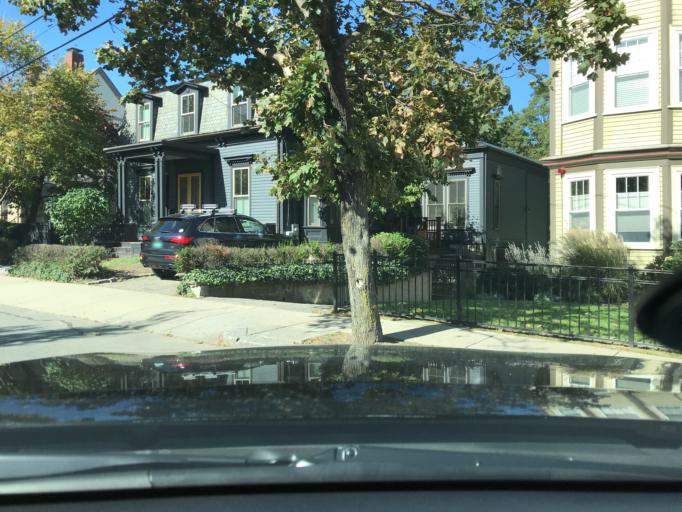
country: US
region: Massachusetts
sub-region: Norfolk County
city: Brookline
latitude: 42.3391
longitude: -71.1167
